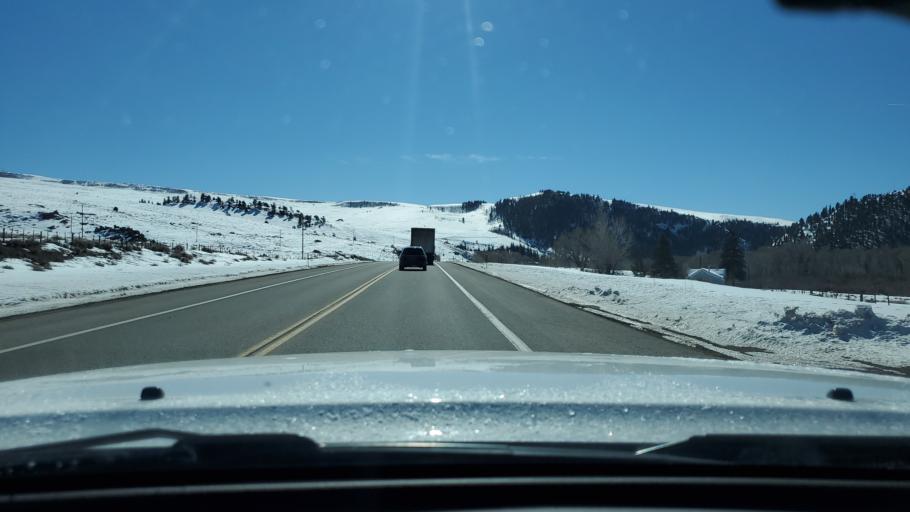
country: US
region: Colorado
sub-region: Gunnison County
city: Gunnison
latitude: 38.6770
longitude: -106.8512
